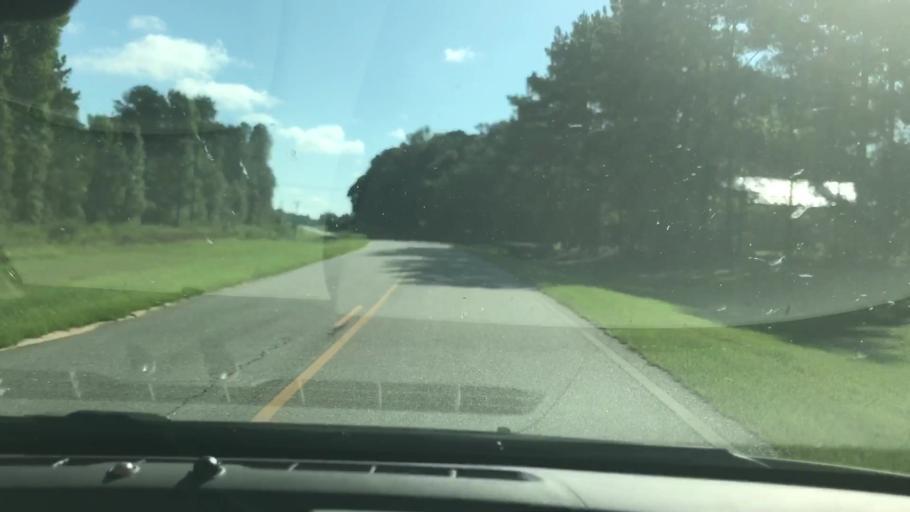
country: US
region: Georgia
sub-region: Clay County
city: Fort Gaines
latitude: 31.7205
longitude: -85.0476
